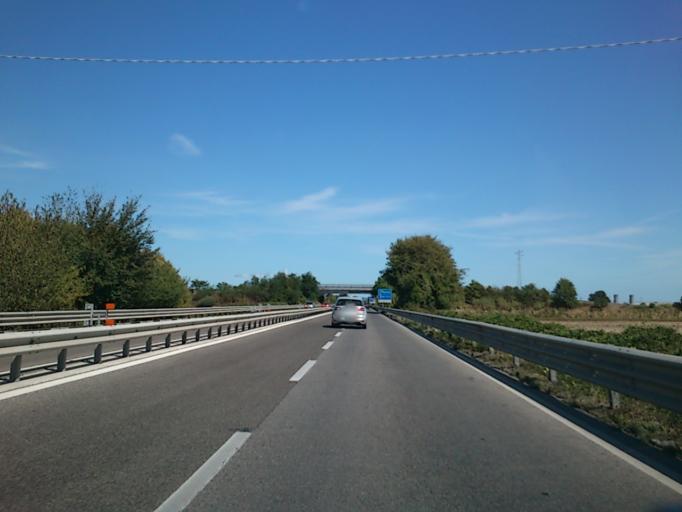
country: IT
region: The Marches
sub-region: Provincia di Pesaro e Urbino
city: Bellocchi
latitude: 43.7816
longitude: 12.9886
